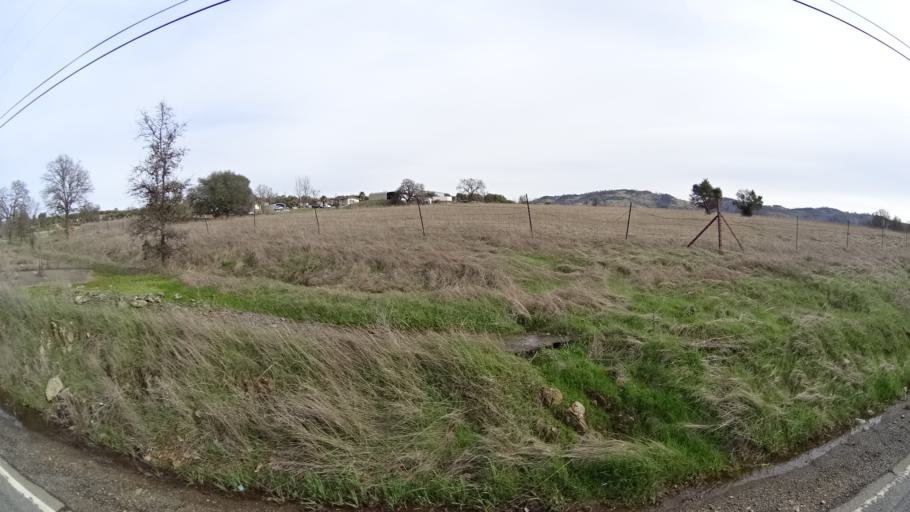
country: US
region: California
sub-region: Butte County
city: Oroville East
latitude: 39.4585
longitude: -121.4483
